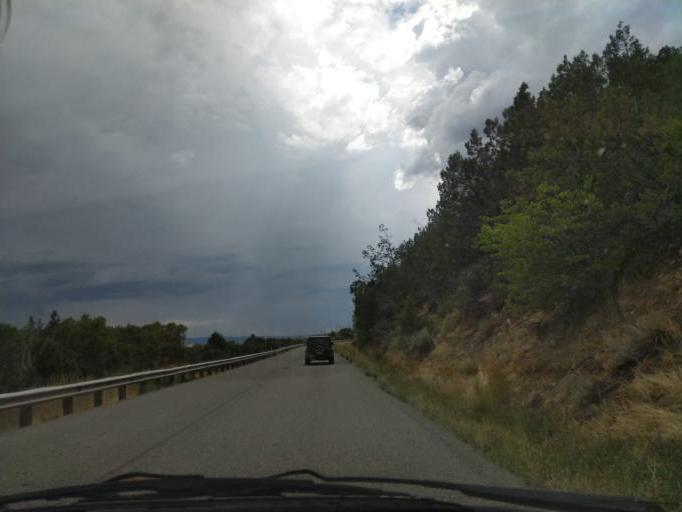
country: US
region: Colorado
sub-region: Delta County
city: Paonia
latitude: 38.8943
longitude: -107.5746
